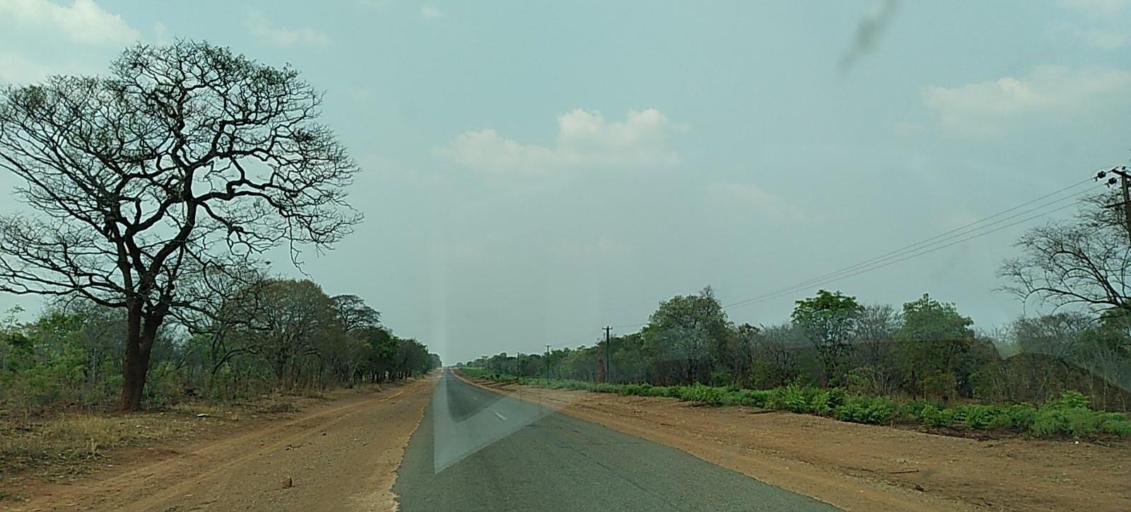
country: ZM
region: North-Western
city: Kabompo
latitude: -13.5774
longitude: 24.2386
